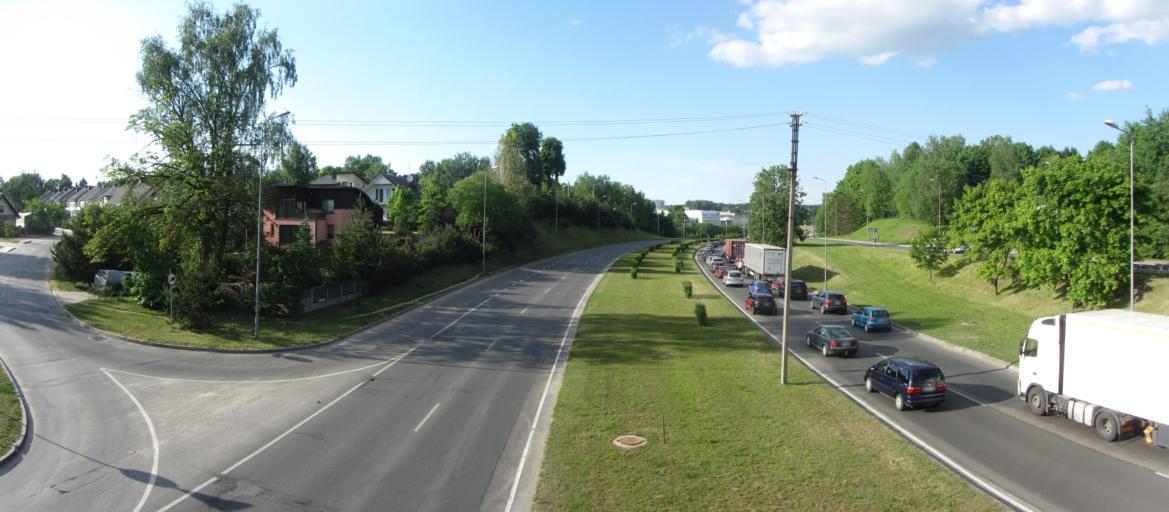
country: LT
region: Vilnius County
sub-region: Vilnius
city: Fabijoniskes
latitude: 54.7460
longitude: 25.2633
